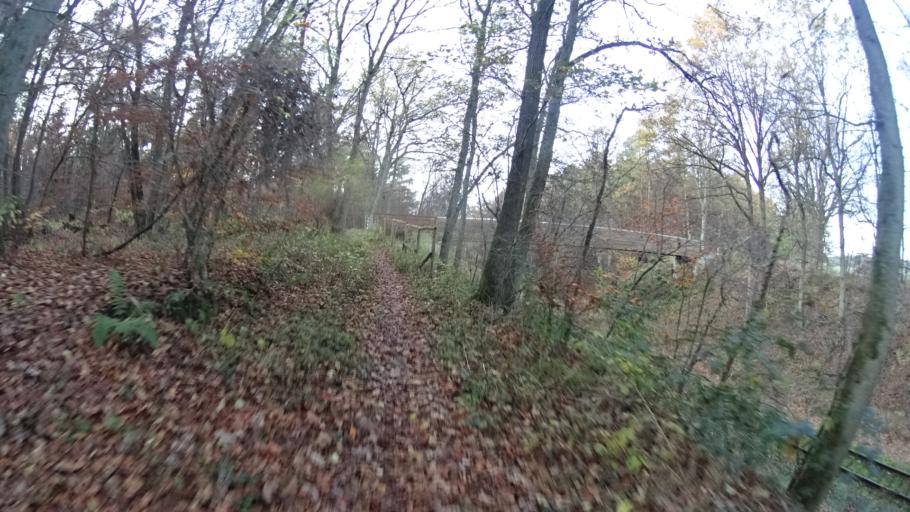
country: DE
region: Lower Saxony
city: Deutsch Evern
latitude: 53.2215
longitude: 10.4377
